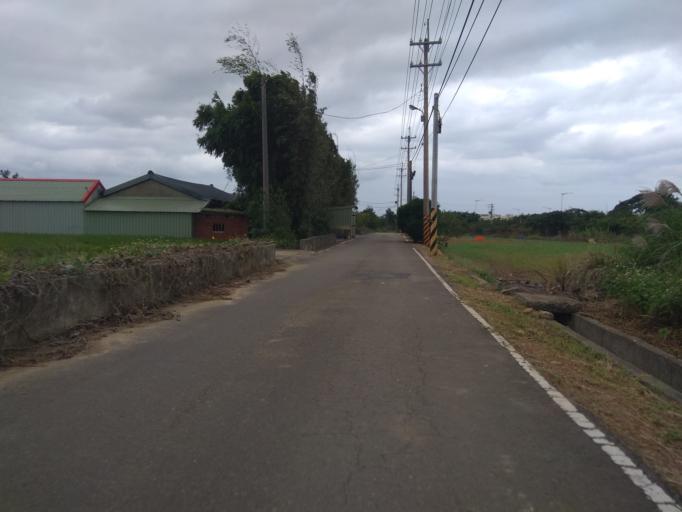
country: TW
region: Taiwan
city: Taoyuan City
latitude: 25.0398
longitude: 121.2216
